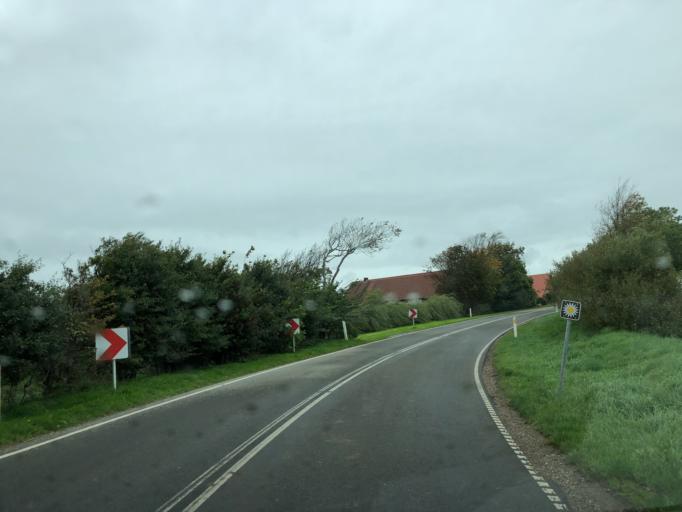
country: DK
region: North Denmark
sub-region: Thisted Kommune
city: Hurup
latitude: 56.7163
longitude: 8.3894
